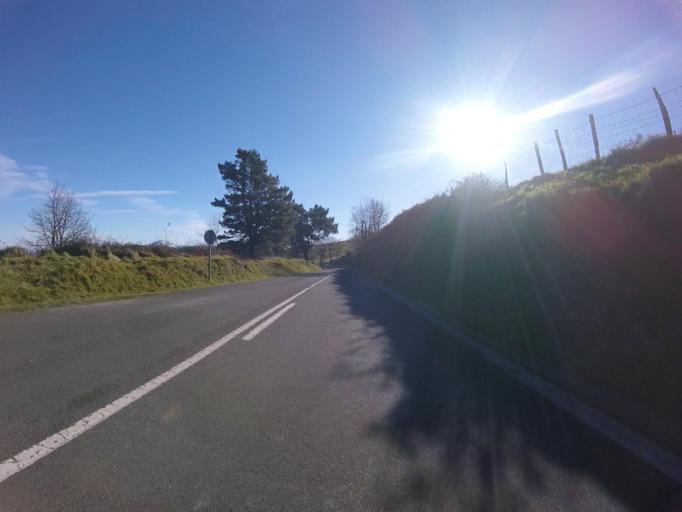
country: ES
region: Basque Country
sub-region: Provincia de Guipuzcoa
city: Lezo
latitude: 43.3505
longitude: -1.8497
